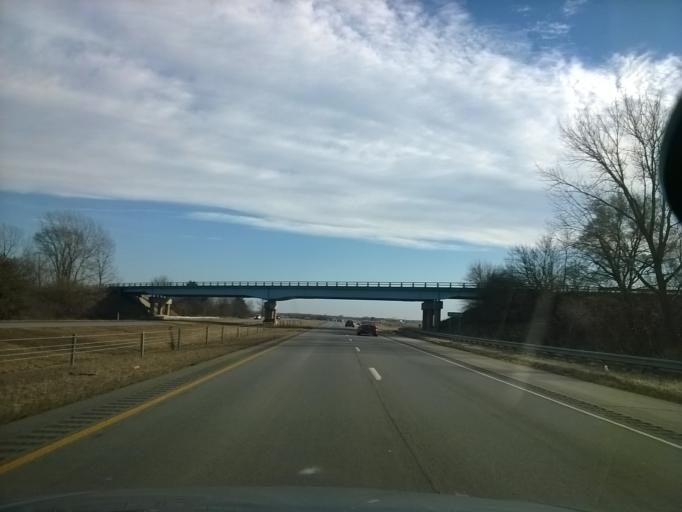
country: US
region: Indiana
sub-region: Johnson County
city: Edinburgh
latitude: 39.4206
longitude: -85.9678
